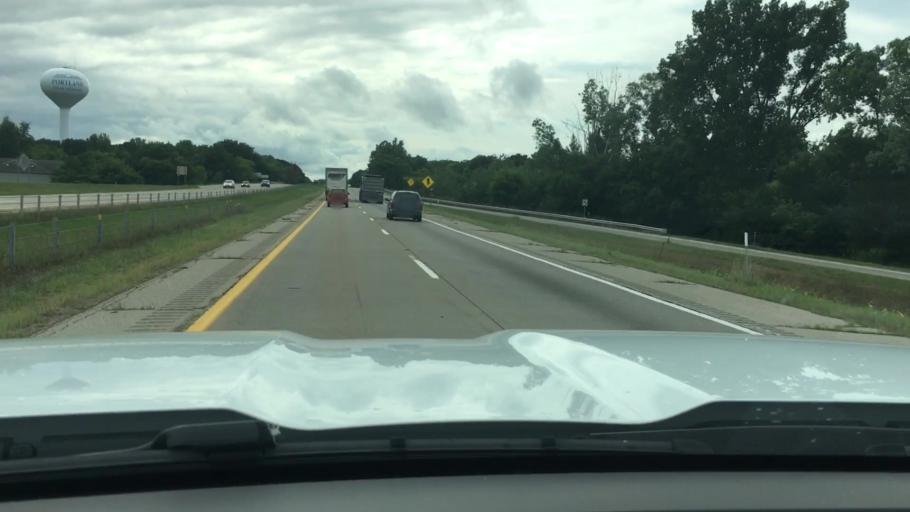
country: US
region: Michigan
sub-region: Ionia County
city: Portland
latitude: 42.8570
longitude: -84.8881
